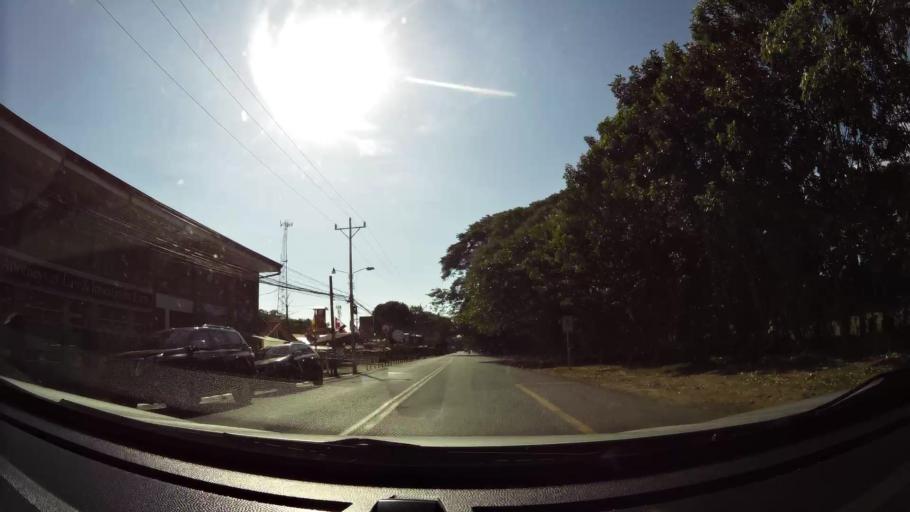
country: CR
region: Puntarenas
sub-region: Canton de Garabito
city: Jaco
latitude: 9.6111
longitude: -84.6197
